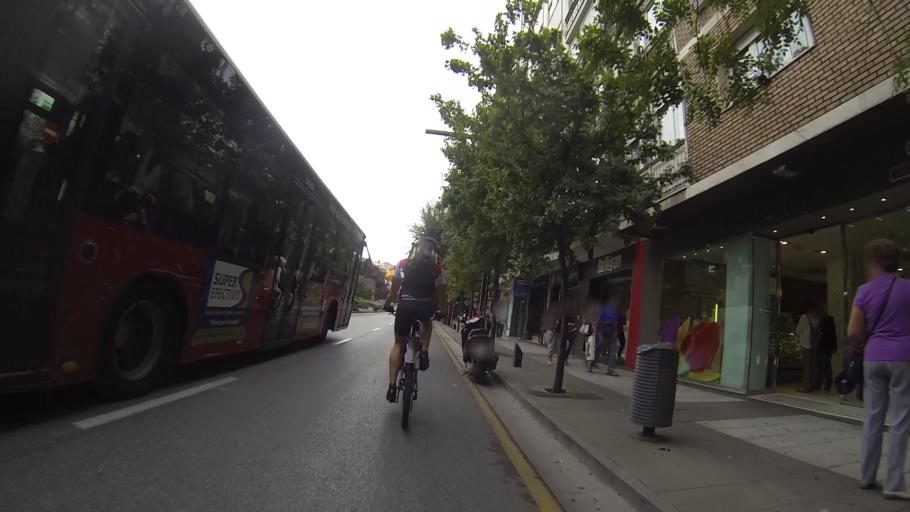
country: ES
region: Andalusia
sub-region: Provincia de Granada
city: Granada
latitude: 37.1839
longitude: -3.6040
